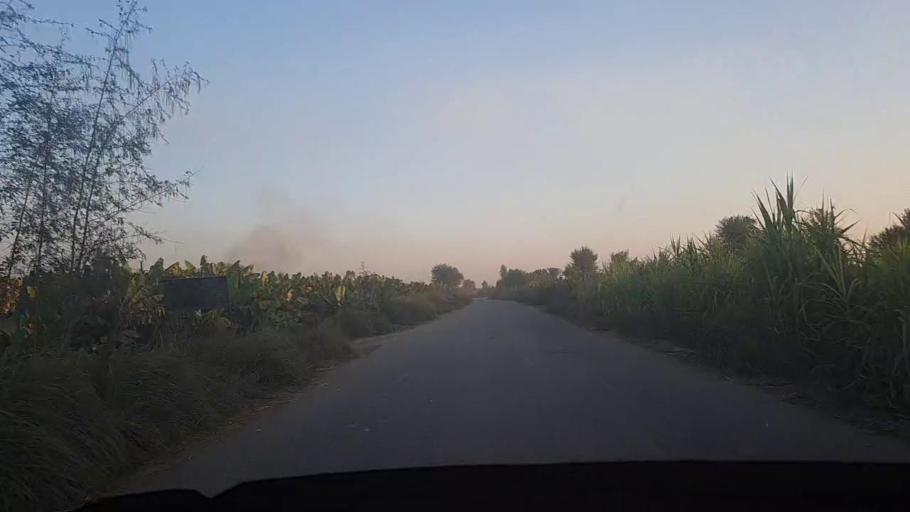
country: PK
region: Sindh
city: Sobhadero
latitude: 27.3455
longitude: 68.3767
